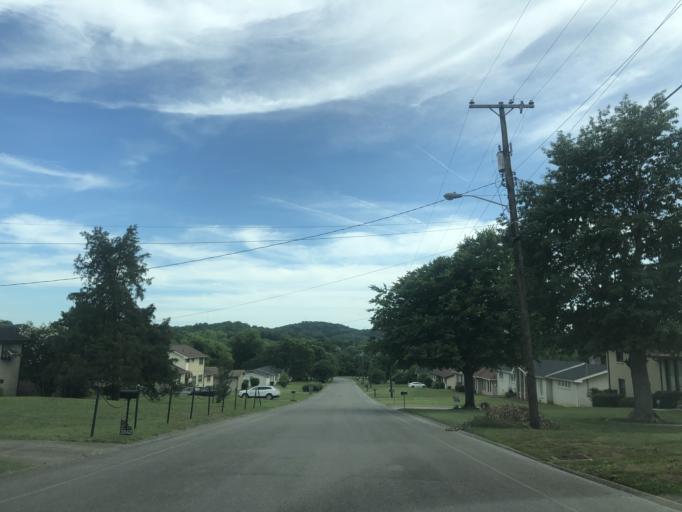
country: US
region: Tennessee
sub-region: Davidson County
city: Nashville
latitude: 36.2224
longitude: -86.8157
